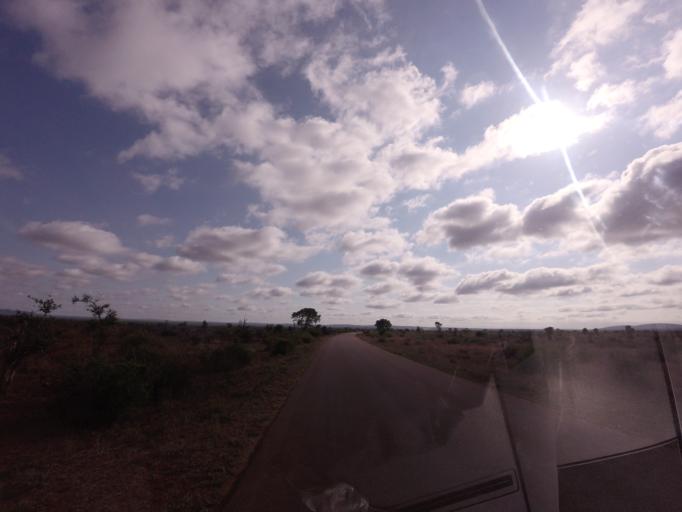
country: ZA
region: Mpumalanga
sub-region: Ehlanzeni District
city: Komatipoort
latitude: -25.1799
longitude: 31.9042
